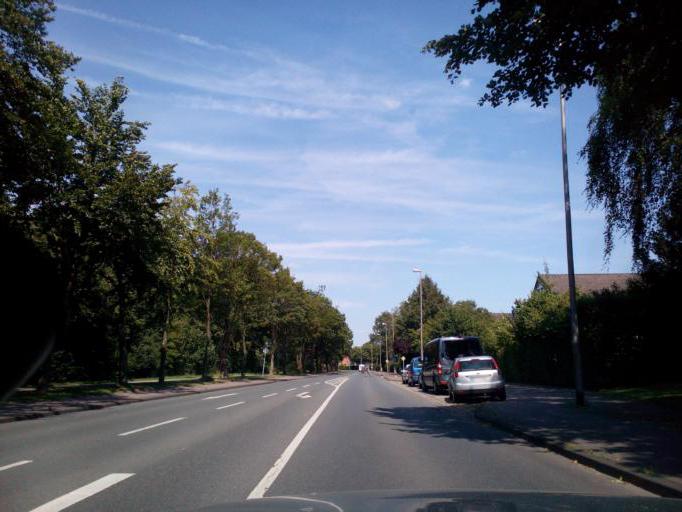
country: DE
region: North Rhine-Westphalia
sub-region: Regierungsbezirk Munster
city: Muenster
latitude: 51.9399
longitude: 7.5928
